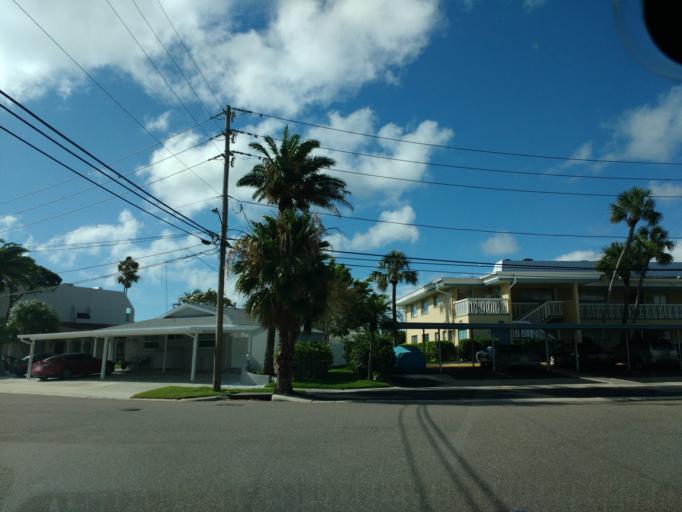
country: US
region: Florida
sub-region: Pinellas County
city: Clearwater
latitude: 27.9817
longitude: -82.8183
